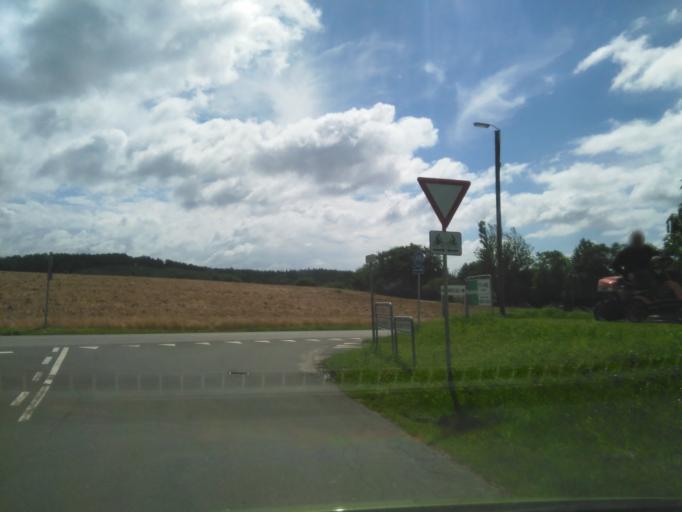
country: DK
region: Central Jutland
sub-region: Syddjurs Kommune
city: Ronde
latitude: 56.2182
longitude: 10.4862
